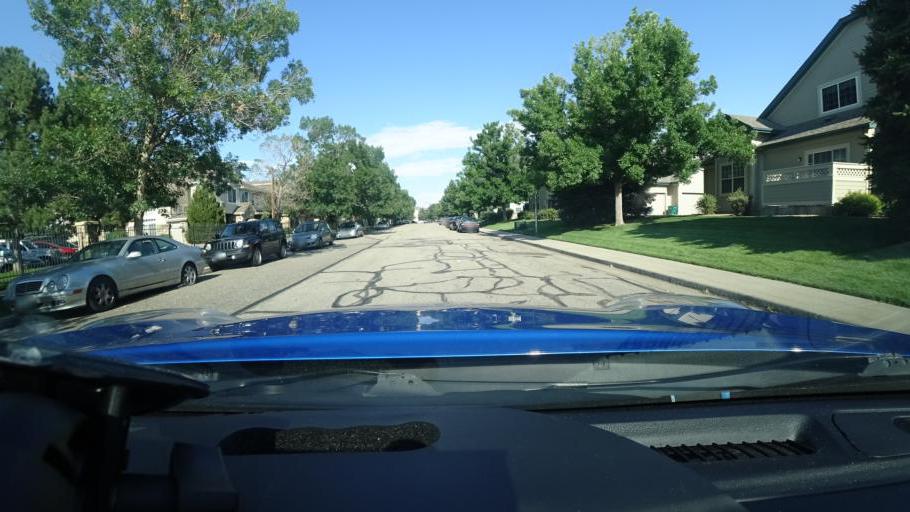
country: US
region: Colorado
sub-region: Adams County
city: Aurora
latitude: 39.6875
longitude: -104.8727
